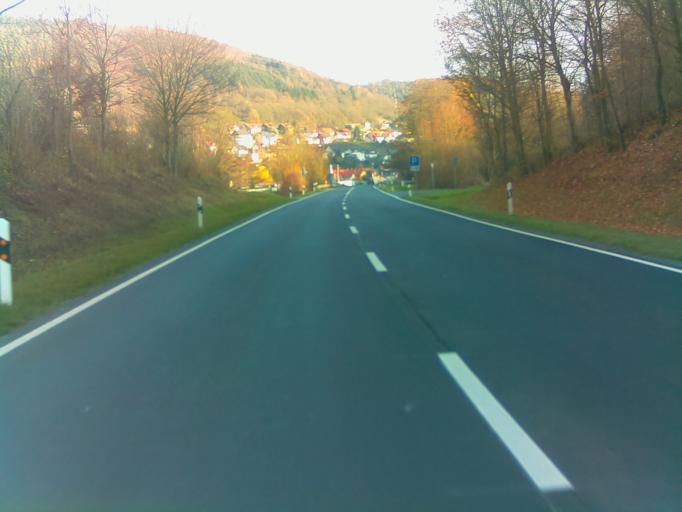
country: DE
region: Bavaria
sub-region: Regierungsbezirk Unterfranken
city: Eichenbuhl
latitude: 49.7073
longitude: 9.3166
